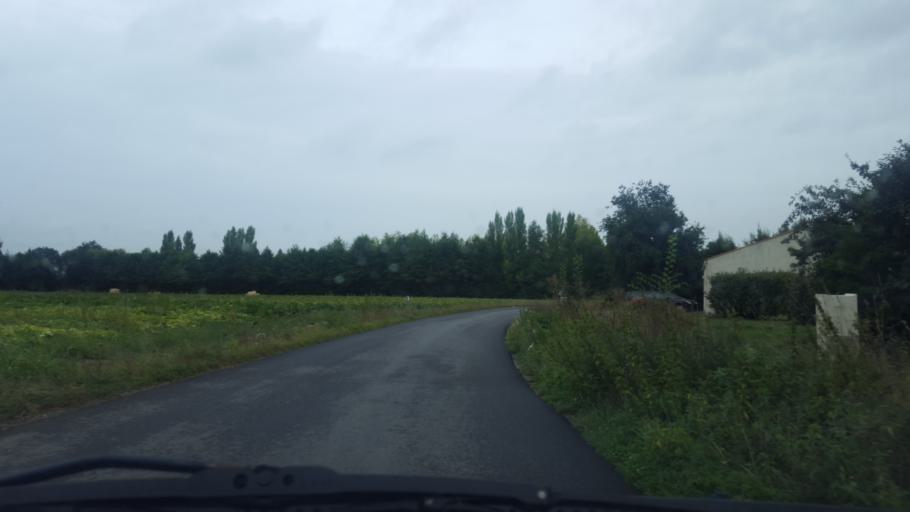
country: FR
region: Pays de la Loire
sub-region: Departement de la Loire-Atlantique
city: Saint-Lumine-de-Coutais
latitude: 47.0515
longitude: -1.6986
